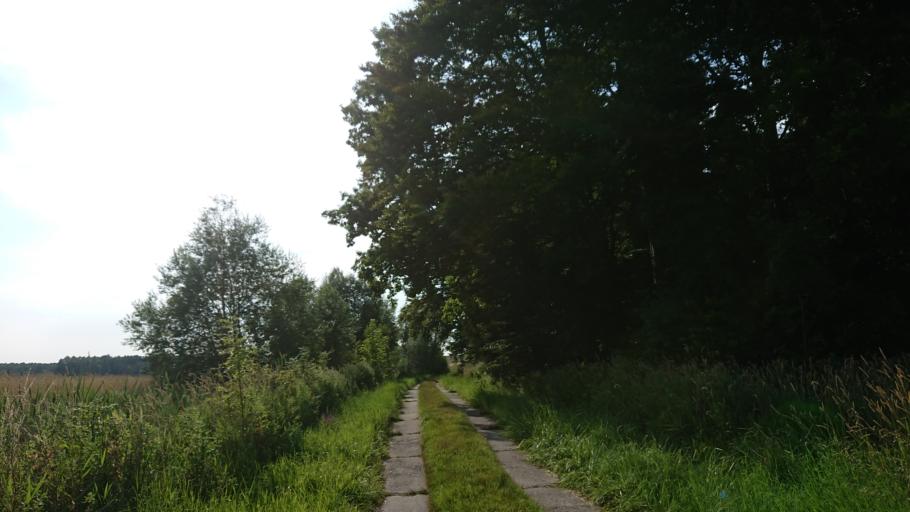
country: DE
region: Mecklenburg-Vorpommern
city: Gormin
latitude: 53.9757
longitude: 13.2870
